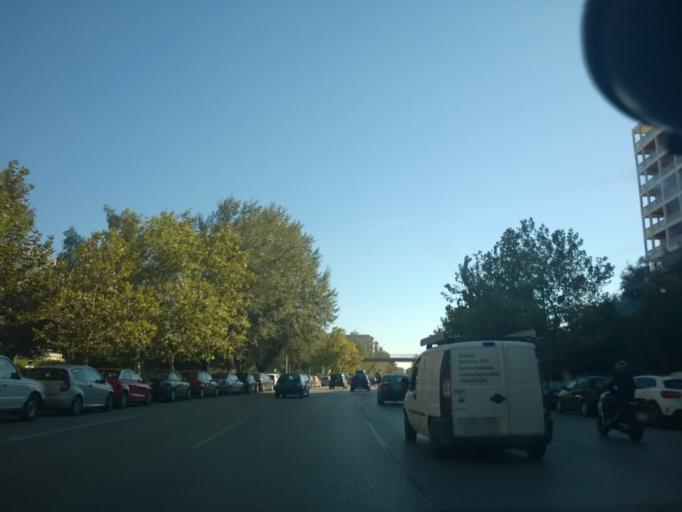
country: GR
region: Central Macedonia
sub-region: Nomos Thessalonikis
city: Triandria
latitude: 40.6183
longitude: 22.9532
